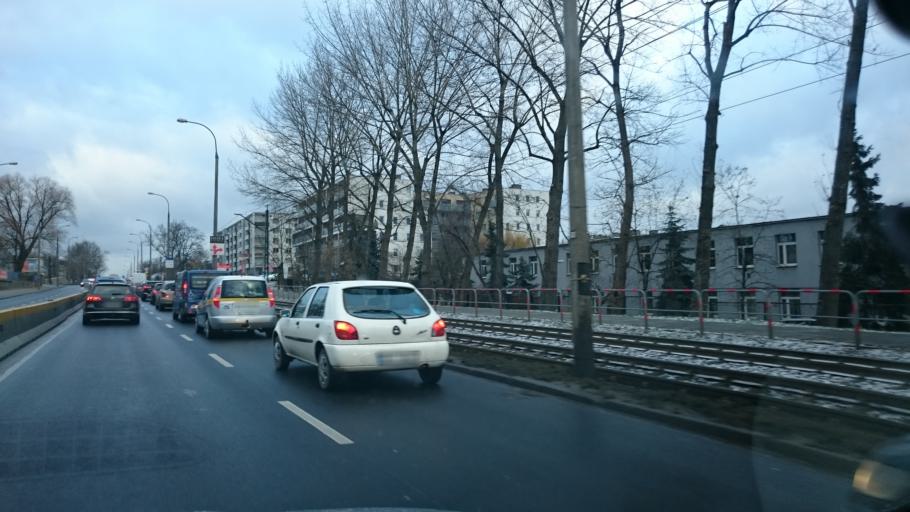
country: PL
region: Lesser Poland Voivodeship
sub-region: Krakow
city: Krakow
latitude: 50.0356
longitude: 19.9679
